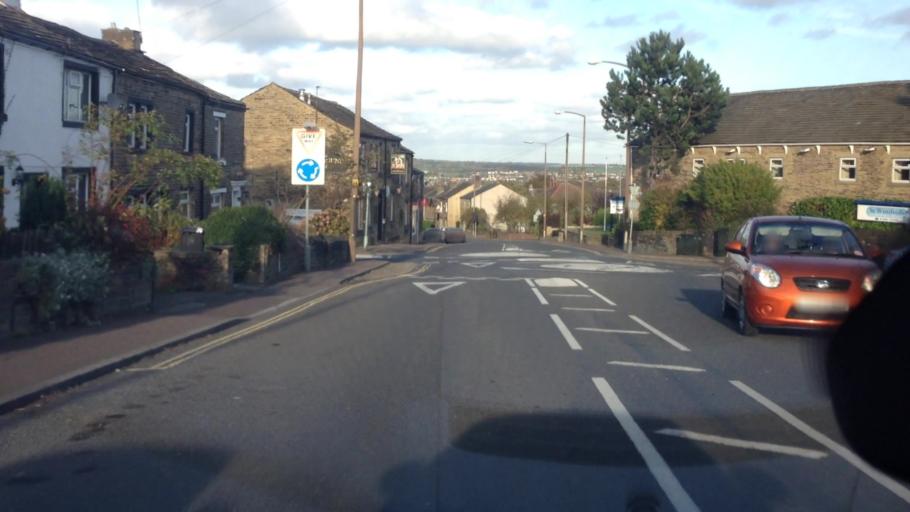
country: GB
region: England
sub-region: Calderdale
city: Brighouse
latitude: 53.6854
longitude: -1.7974
